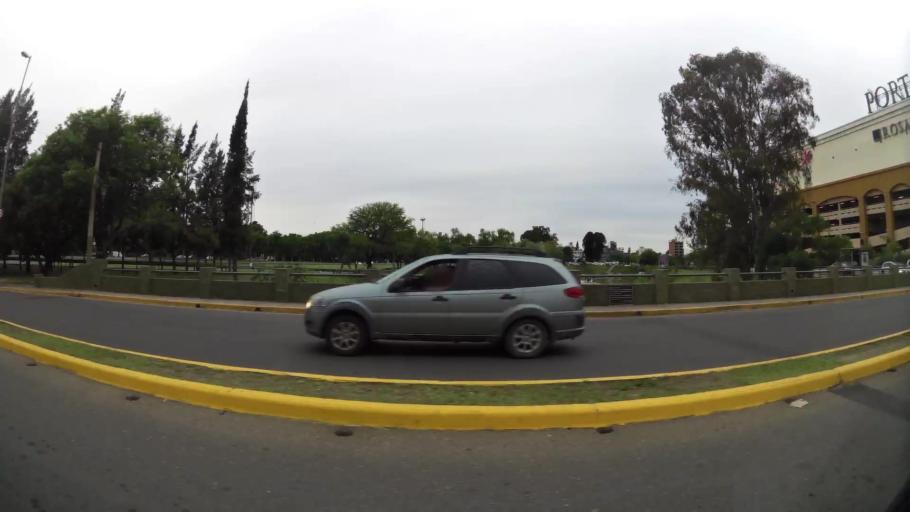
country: AR
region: Santa Fe
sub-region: Departamento de Rosario
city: Rosario
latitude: -32.9092
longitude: -60.6815
